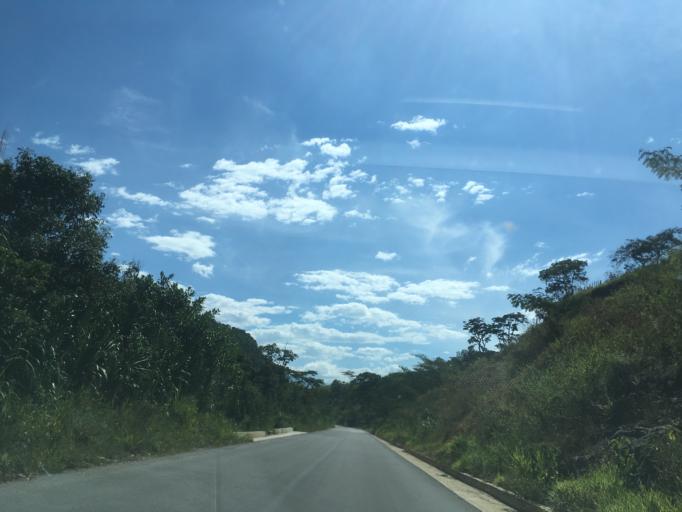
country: CO
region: Santander
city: Coromoro
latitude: 6.3069
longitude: -73.1434
